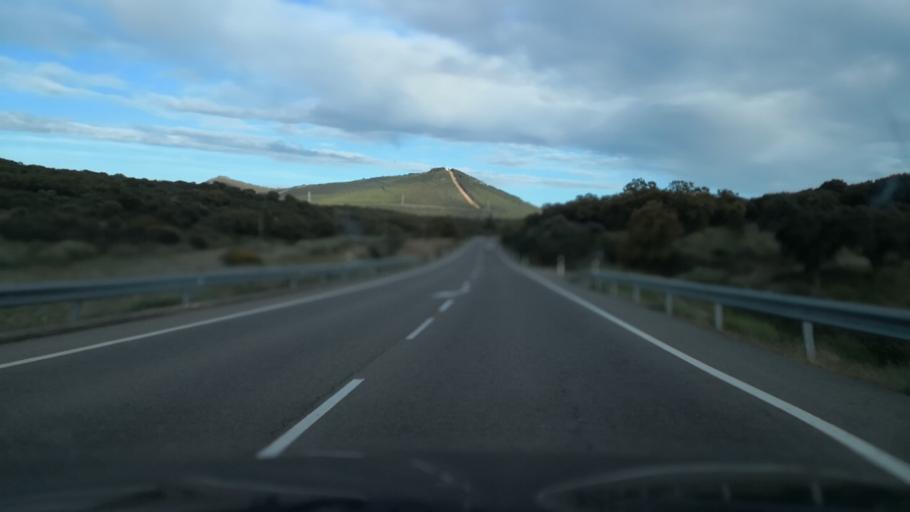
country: ES
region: Extremadura
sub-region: Provincia de Caceres
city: Pedroso de Acim
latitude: 39.8336
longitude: -6.3891
